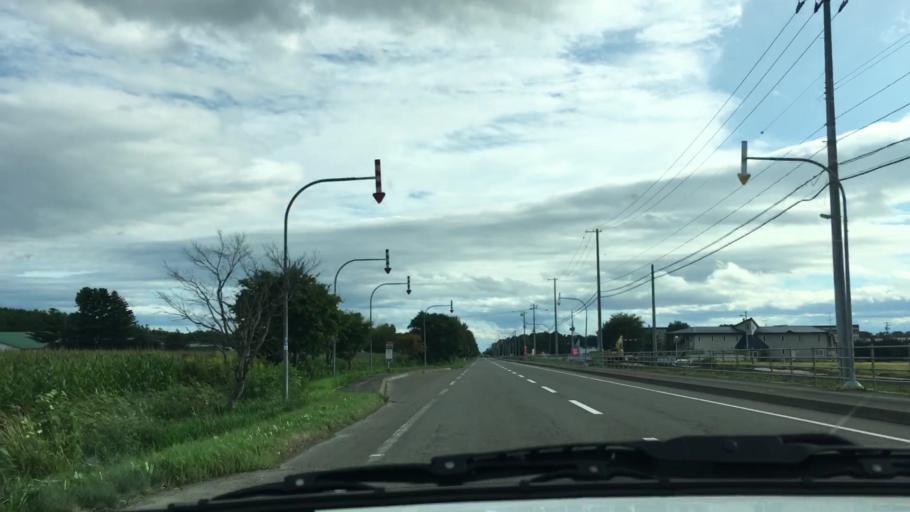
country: JP
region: Hokkaido
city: Otofuke
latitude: 43.2545
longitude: 143.3000
